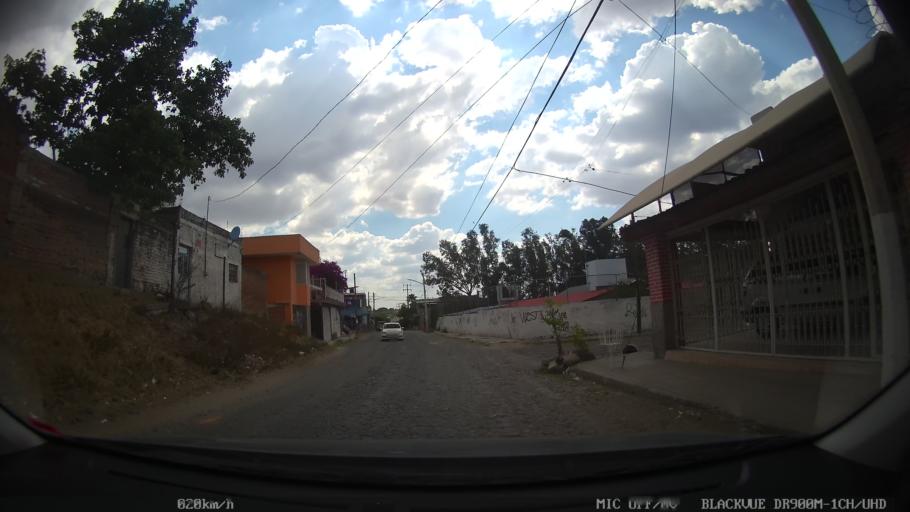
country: MX
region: Jalisco
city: Tlaquepaque
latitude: 20.6836
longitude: -103.2625
